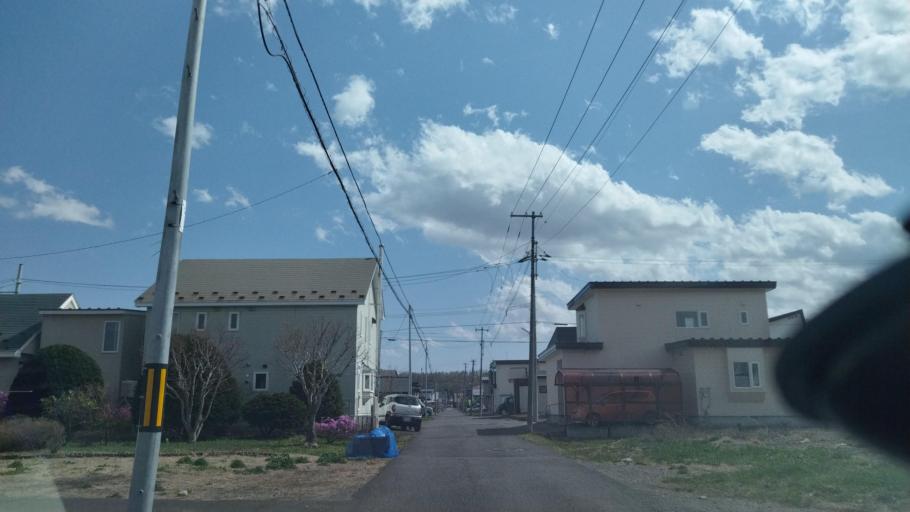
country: JP
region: Hokkaido
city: Obihiro
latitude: 42.9077
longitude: 143.1588
